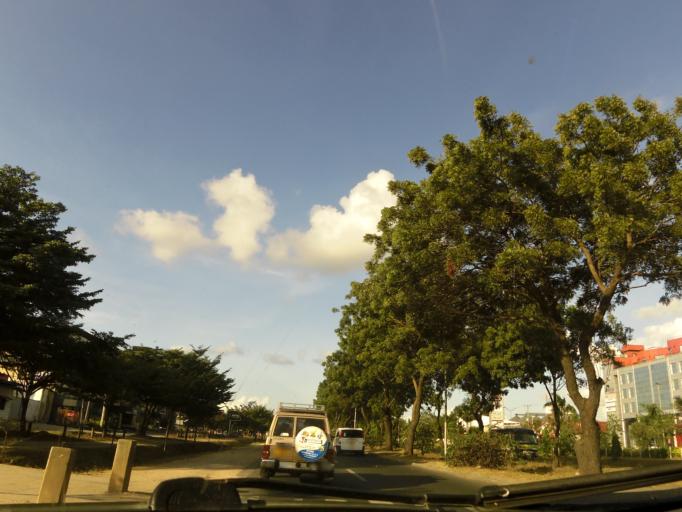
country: TZ
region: Dar es Salaam
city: Dar es Salaam
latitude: -6.8363
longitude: 39.2610
